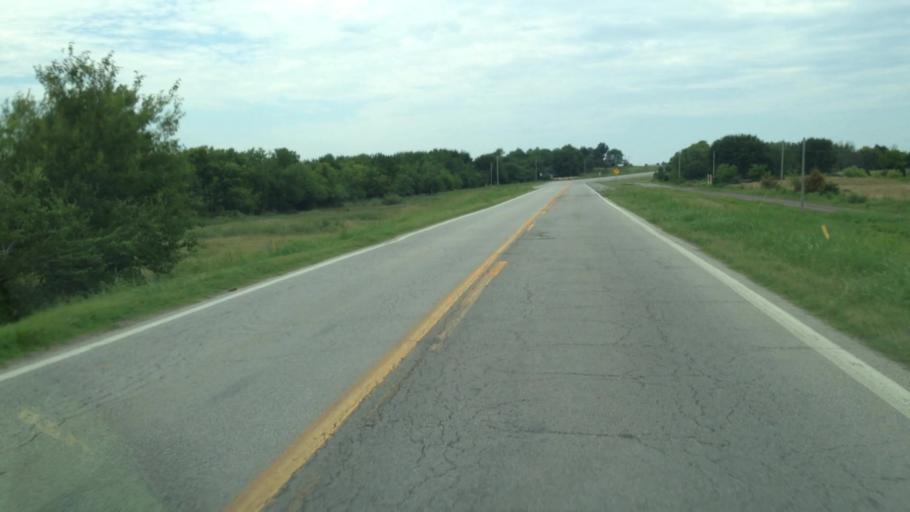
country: US
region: Kansas
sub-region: Labette County
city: Chetopa
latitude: 36.8824
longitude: -95.0989
